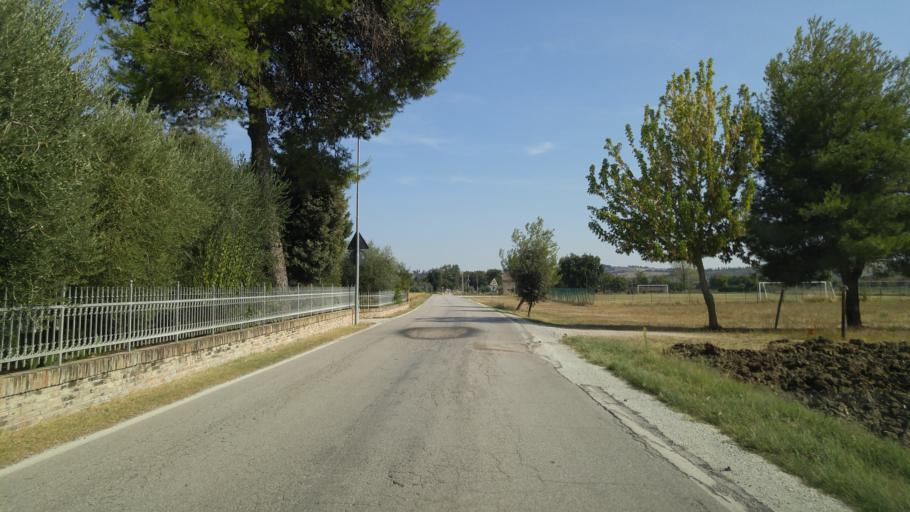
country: IT
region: The Marches
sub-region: Provincia di Pesaro e Urbino
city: Bellocchi
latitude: 43.7938
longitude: 12.9889
